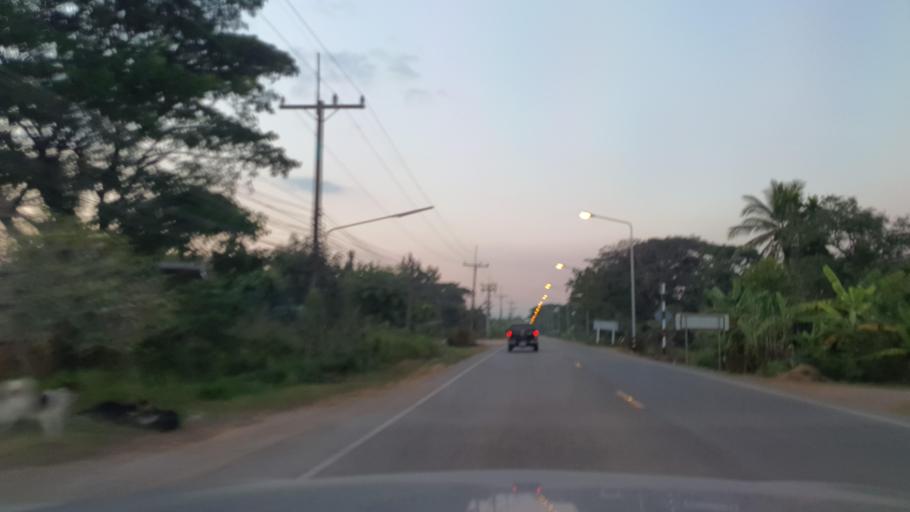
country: TH
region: Phayao
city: Dok Kham Tai
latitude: 19.0921
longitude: 100.0651
